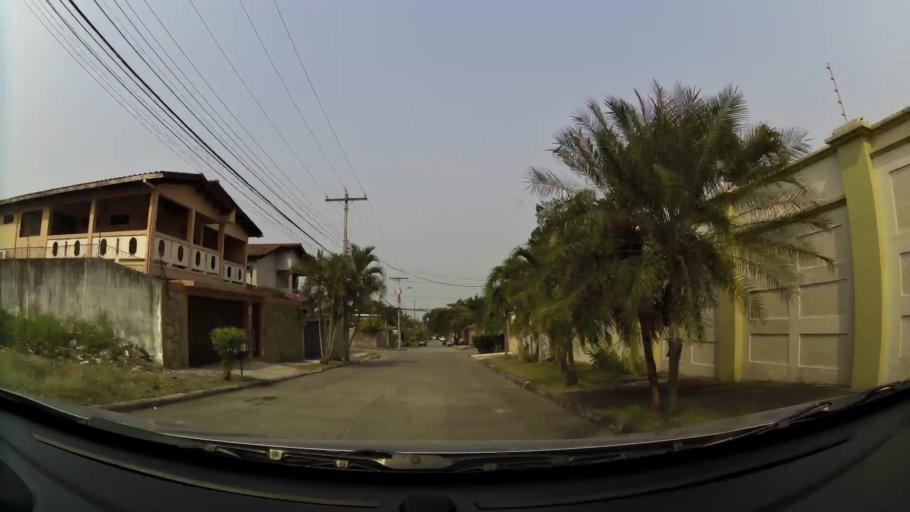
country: HN
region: Cortes
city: Armenta
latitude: 15.4930
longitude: -88.0452
